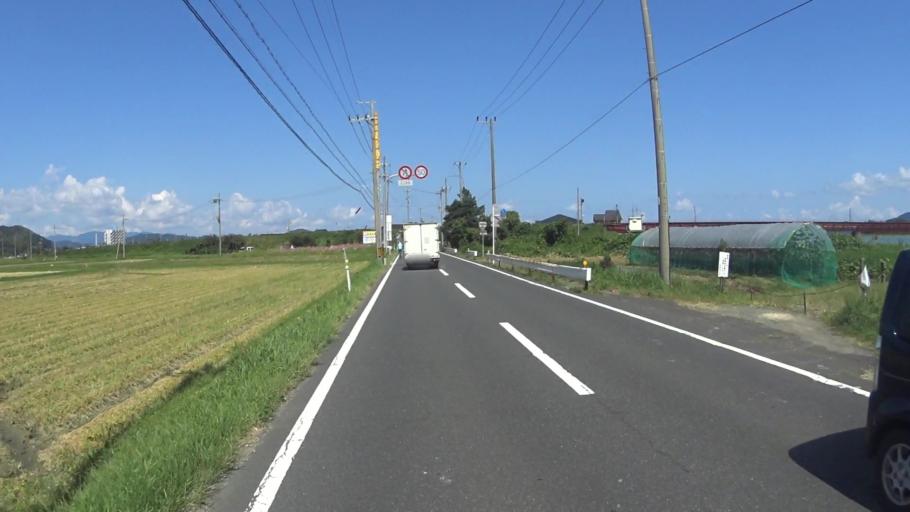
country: JP
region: Kyoto
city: Maizuru
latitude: 35.5109
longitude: 135.2845
